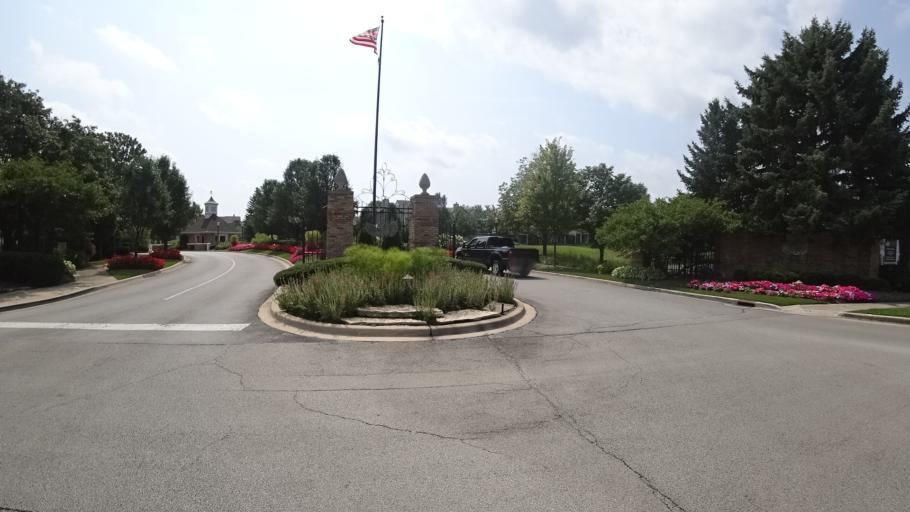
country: US
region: Illinois
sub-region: Cook County
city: Orland Park
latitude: 41.6299
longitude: -87.8760
